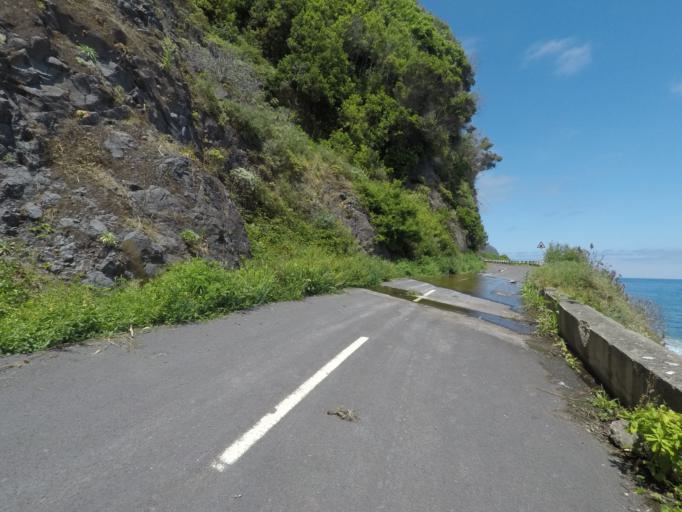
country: PT
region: Madeira
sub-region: Porto Moniz
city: Porto Moniz
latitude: 32.8292
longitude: -17.1280
